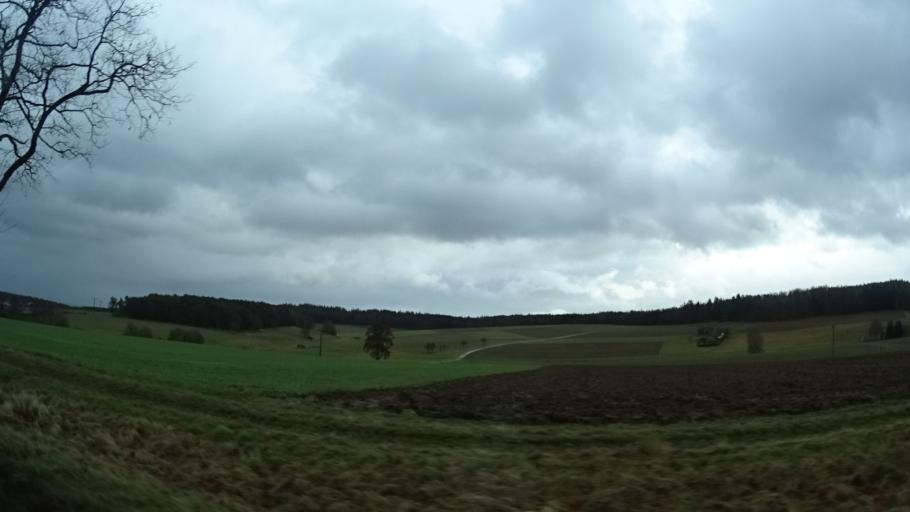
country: DE
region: Hesse
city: Grebenau
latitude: 50.6771
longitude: 9.4639
